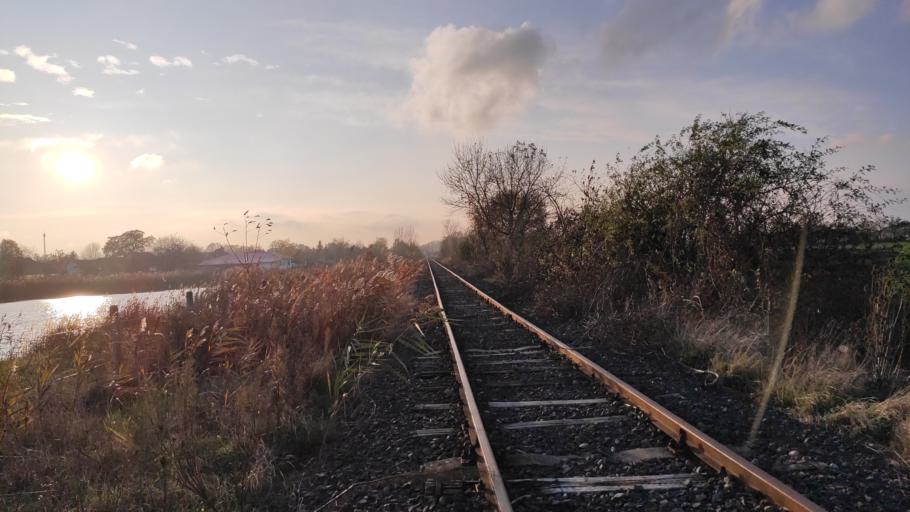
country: HU
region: Bekes
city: Mezobereny
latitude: 46.7649
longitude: 21.0479
